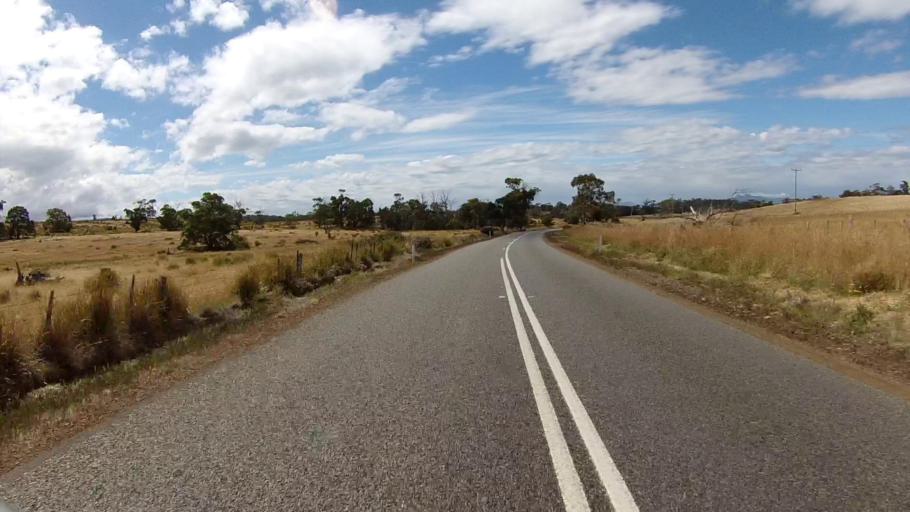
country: AU
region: Tasmania
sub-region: Sorell
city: Sorell
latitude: -42.2986
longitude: 147.9827
